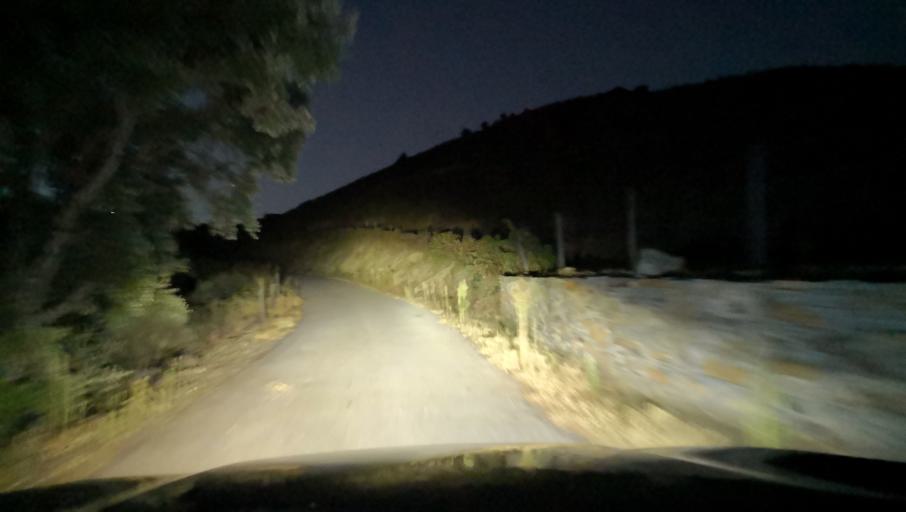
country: PT
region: Viseu
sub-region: Armamar
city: Armamar
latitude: 41.1525
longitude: -7.6957
